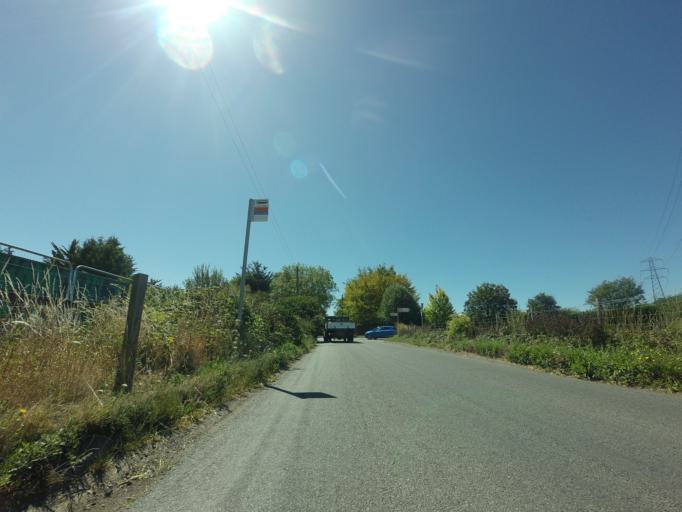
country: GB
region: England
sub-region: Kent
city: Eastry
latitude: 51.2533
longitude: 1.3075
